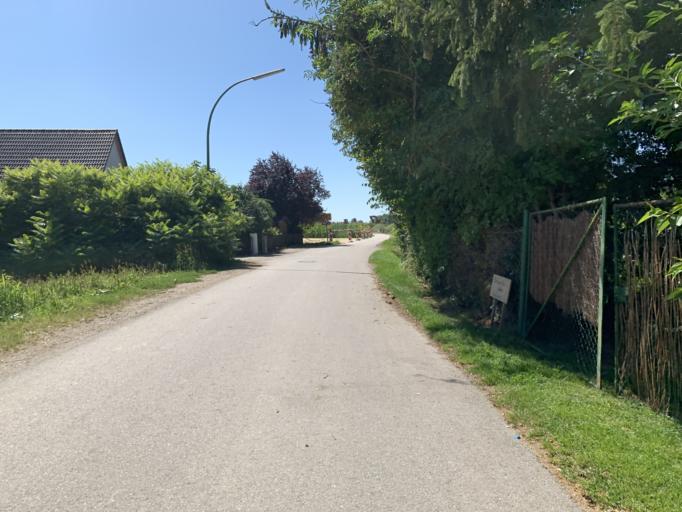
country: DE
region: Bavaria
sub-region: Upper Bavaria
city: Freising
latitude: 48.3871
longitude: 11.7269
